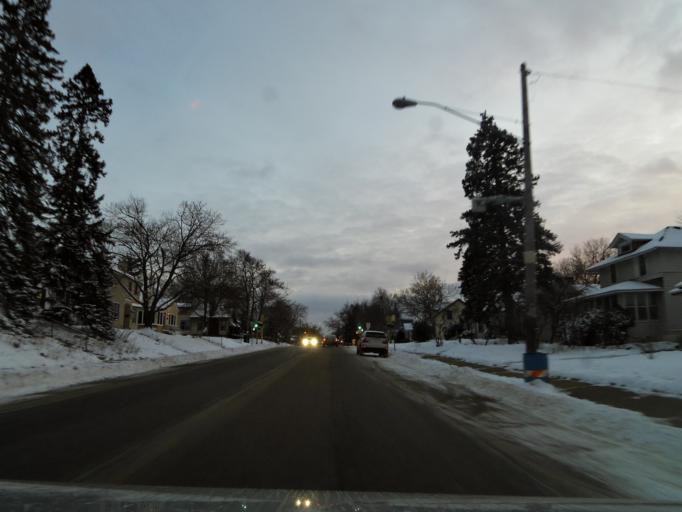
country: US
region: Minnesota
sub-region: Hennepin County
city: Edina
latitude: 44.9149
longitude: -93.3189
